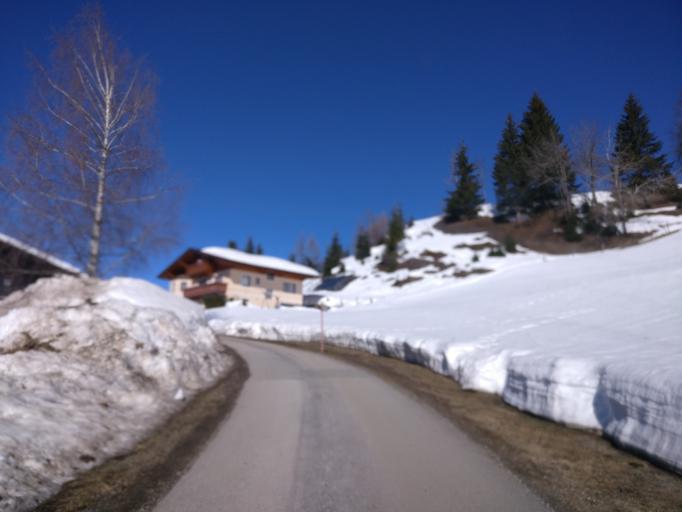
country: AT
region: Salzburg
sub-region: Politischer Bezirk Sankt Johann im Pongau
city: Sankt Johann im Pongau
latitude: 47.3384
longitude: 13.2255
